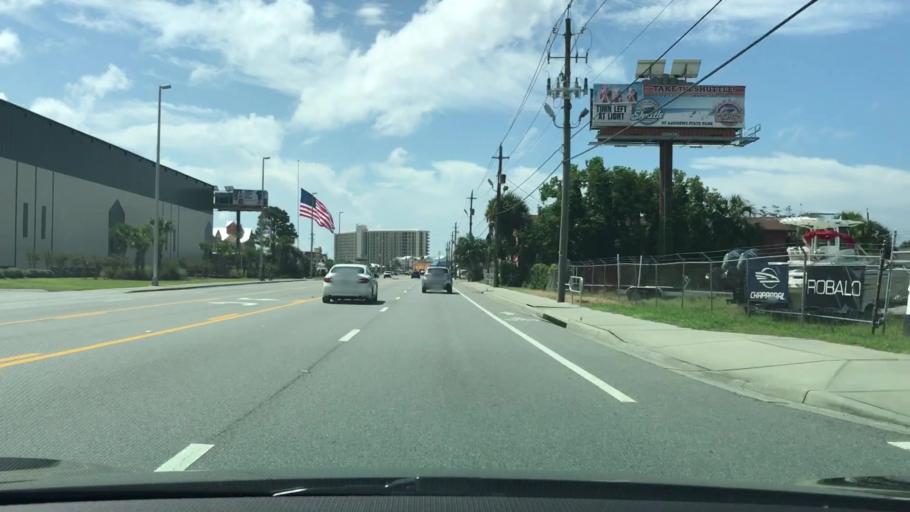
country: US
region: Florida
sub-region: Bay County
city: Lower Grand Lagoon
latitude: 30.1436
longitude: -85.7496
